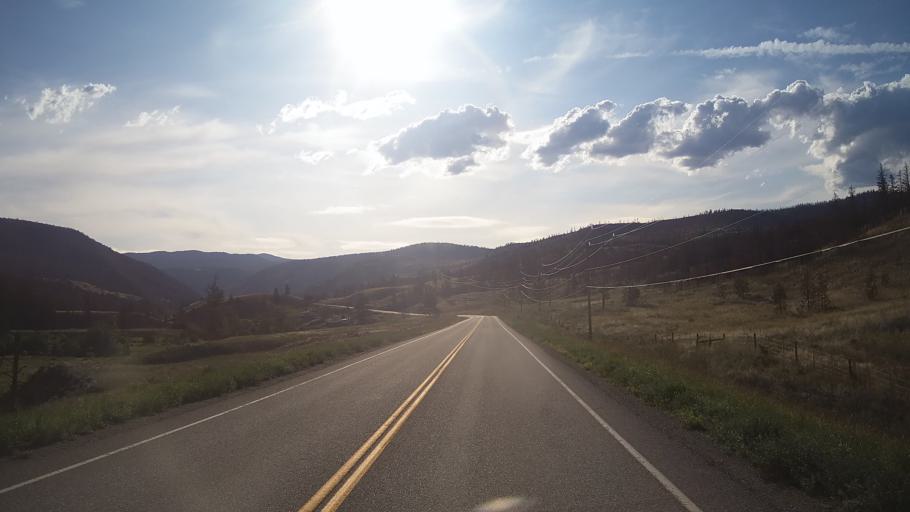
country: CA
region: British Columbia
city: Cache Creek
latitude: 50.8871
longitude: -121.4457
